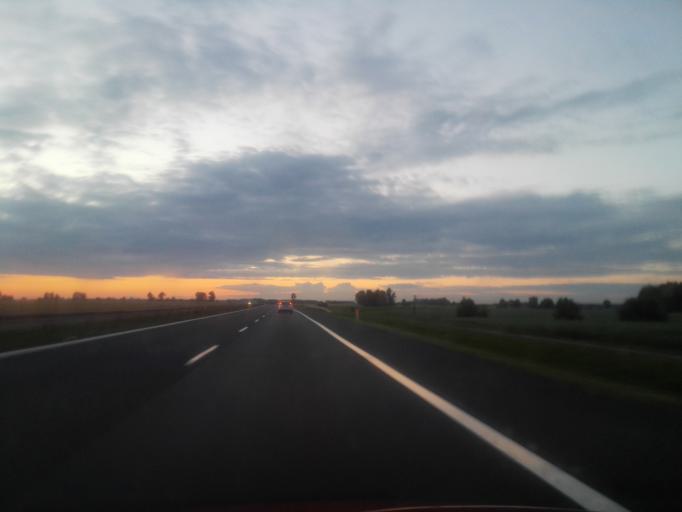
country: PL
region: Lodz Voivodeship
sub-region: Piotrkow Trybunalski
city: Piotrkow Trybunalski
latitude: 51.4563
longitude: 19.6398
